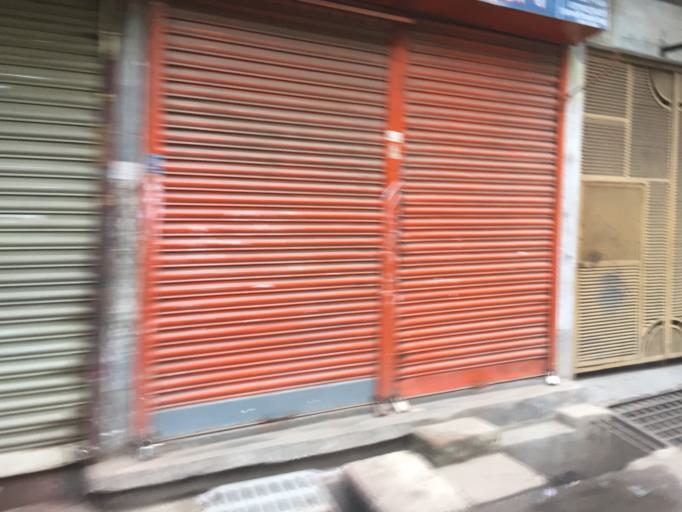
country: BD
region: Dhaka
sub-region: Dhaka
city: Dhaka
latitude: 23.7189
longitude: 90.4069
